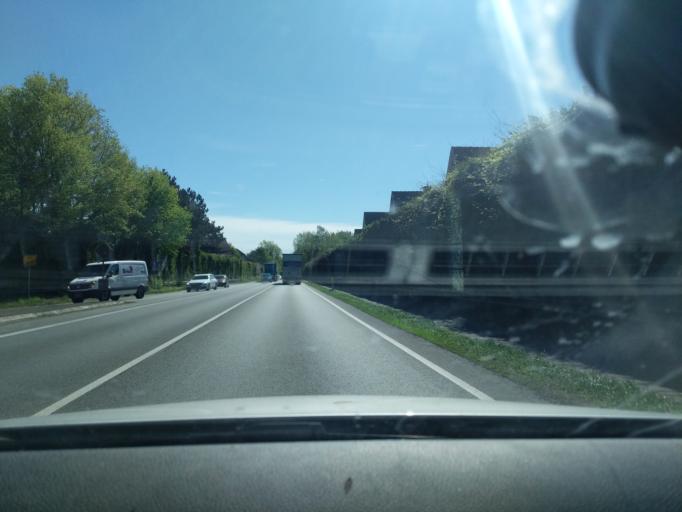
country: DE
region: Lower Saxony
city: Buxtehude
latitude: 53.4648
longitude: 9.6824
